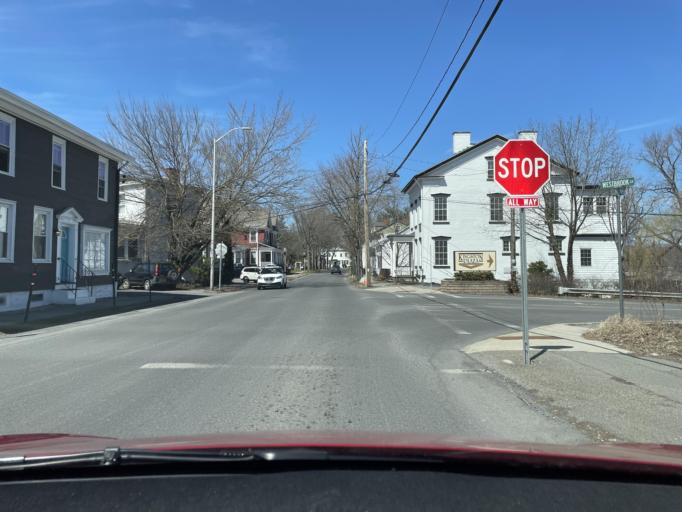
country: US
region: New York
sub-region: Ulster County
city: Kingston
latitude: 41.9338
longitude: -74.0169
